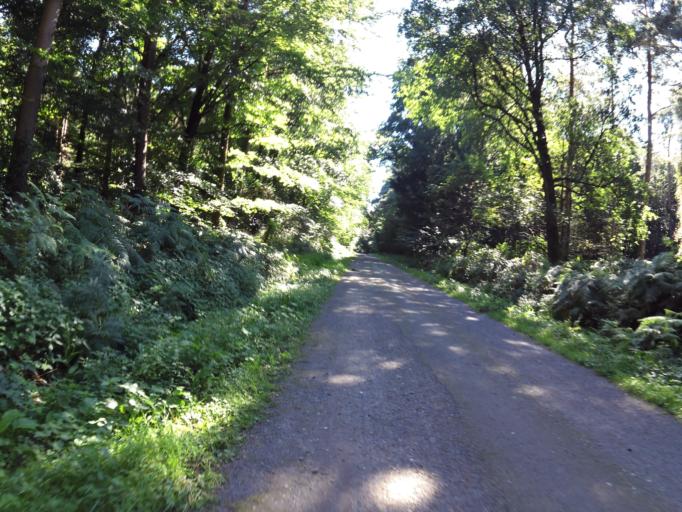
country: NL
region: Gelderland
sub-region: Gemeente Groesbeek
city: De Horst
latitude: 51.7485
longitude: 5.9886
